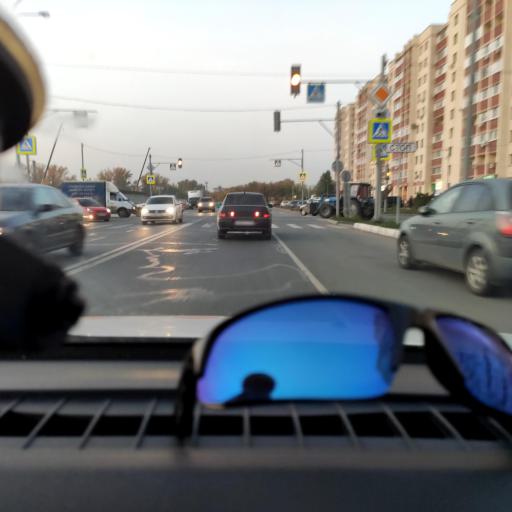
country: RU
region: Samara
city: Rozhdestveno
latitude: 53.1557
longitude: 50.0755
